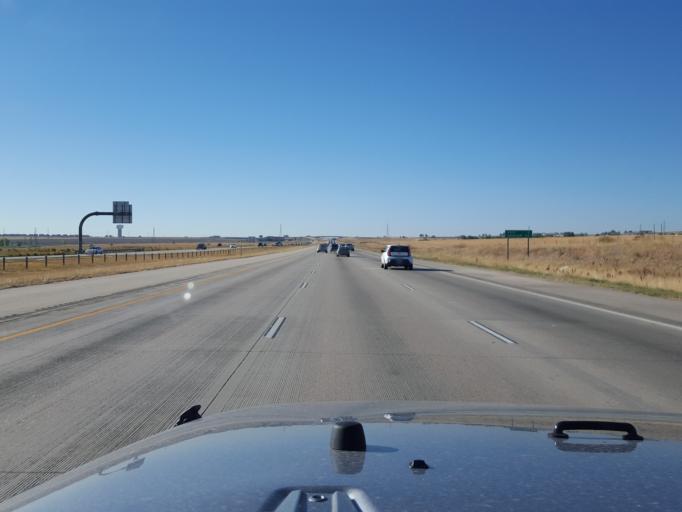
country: US
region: Colorado
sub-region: Weld County
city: Dacono
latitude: 40.0707
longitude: -104.9807
